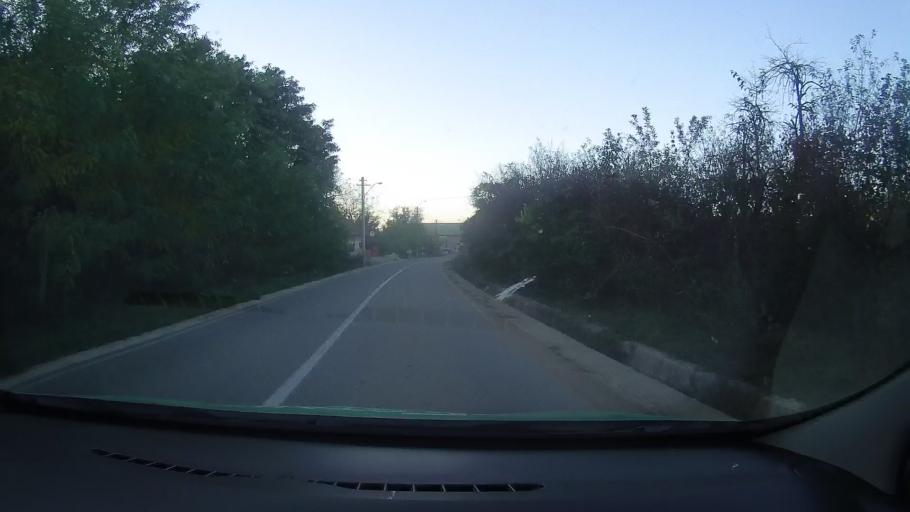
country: RO
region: Timis
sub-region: Comuna Traian Vuia
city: Traian Vuia
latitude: 45.7641
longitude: 22.0957
